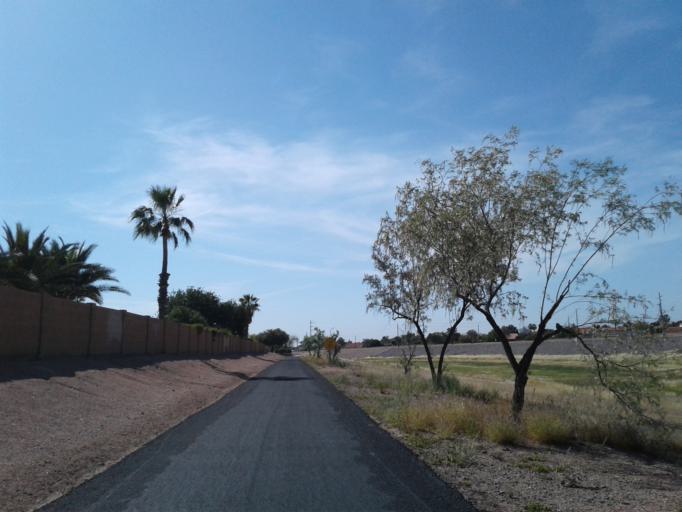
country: US
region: Arizona
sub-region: Maricopa County
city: Peoria
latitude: 33.6024
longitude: -112.1775
